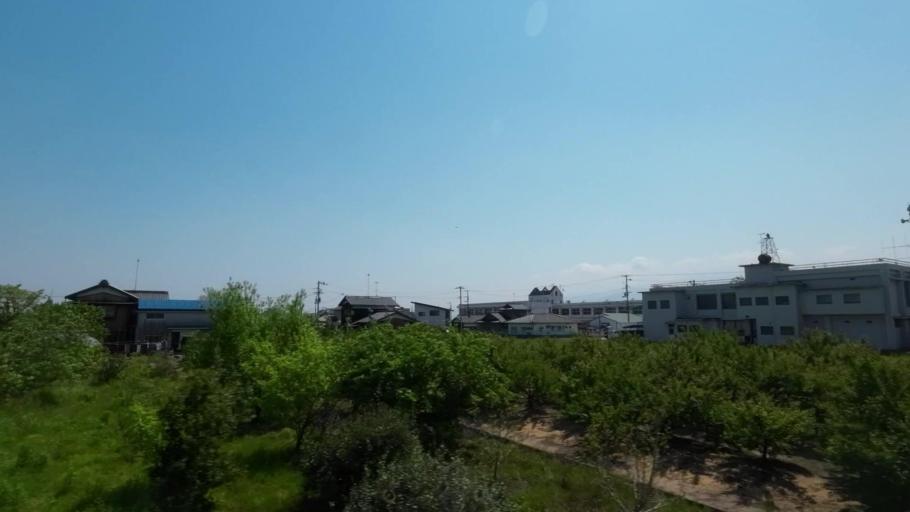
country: JP
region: Ehime
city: Saijo
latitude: 33.9136
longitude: 133.0990
